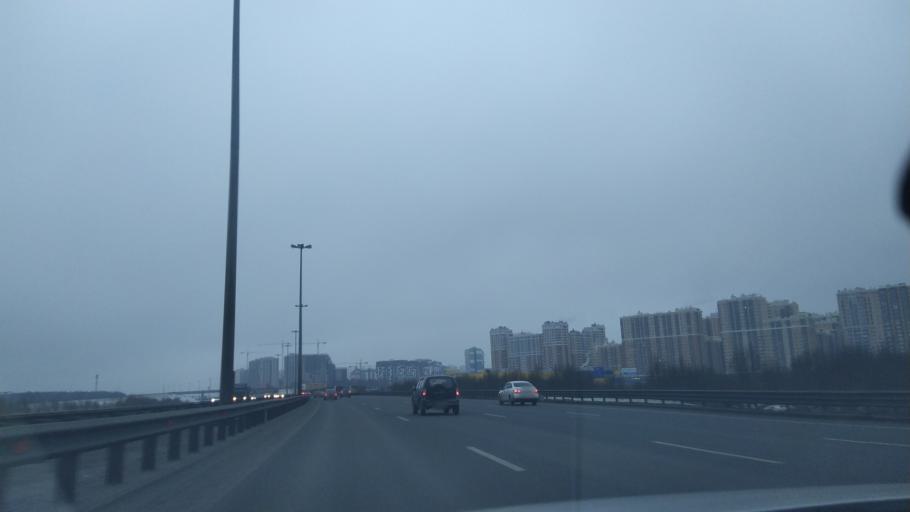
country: RU
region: St.-Petersburg
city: Krasnogvargeisky
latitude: 59.9217
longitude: 30.5274
